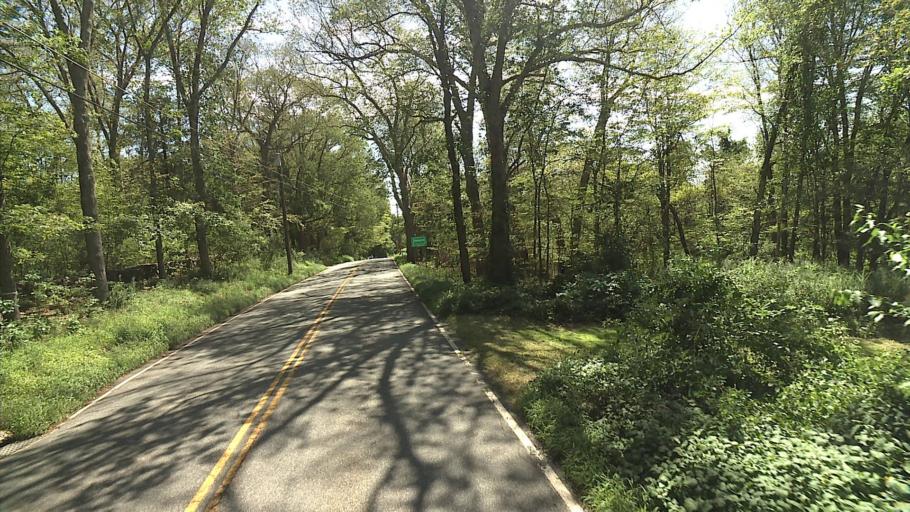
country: US
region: Connecticut
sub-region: Windham County
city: South Woodstock
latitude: 41.8630
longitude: -72.0067
